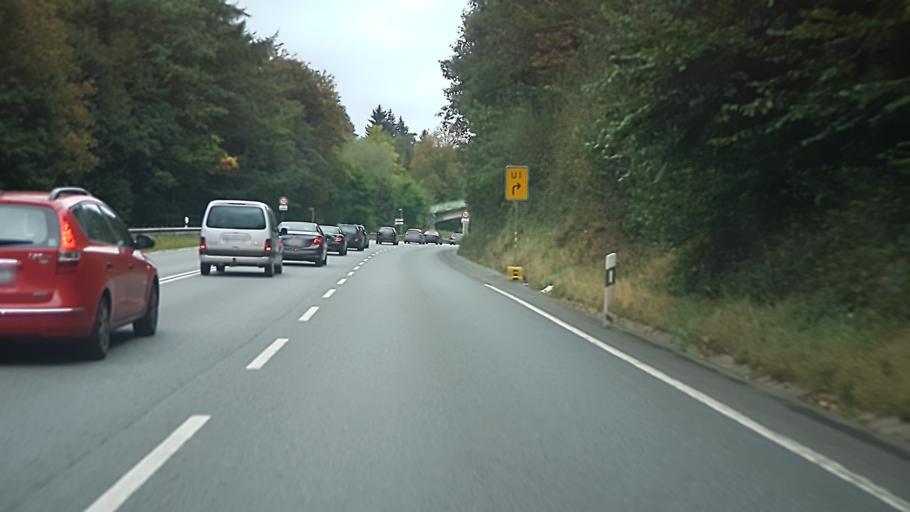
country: DE
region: North Rhine-Westphalia
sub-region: Regierungsbezirk Arnsberg
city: Attendorn
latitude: 51.1145
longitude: 7.8817
